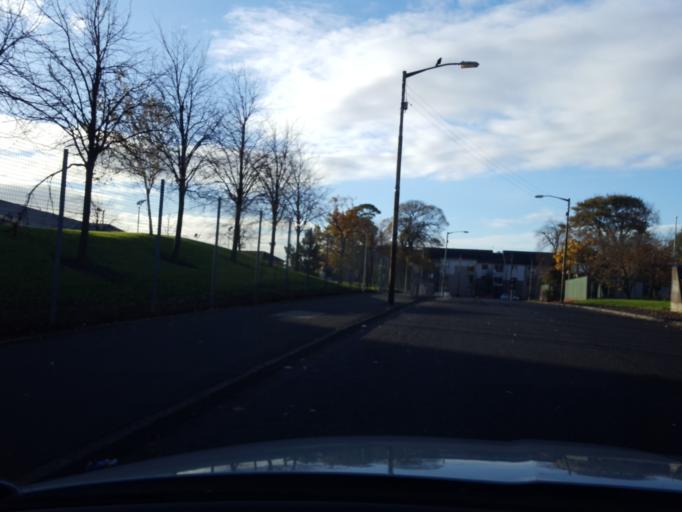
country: GB
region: Scotland
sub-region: North Lanarkshire
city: Chryston
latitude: 55.8691
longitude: -4.1087
